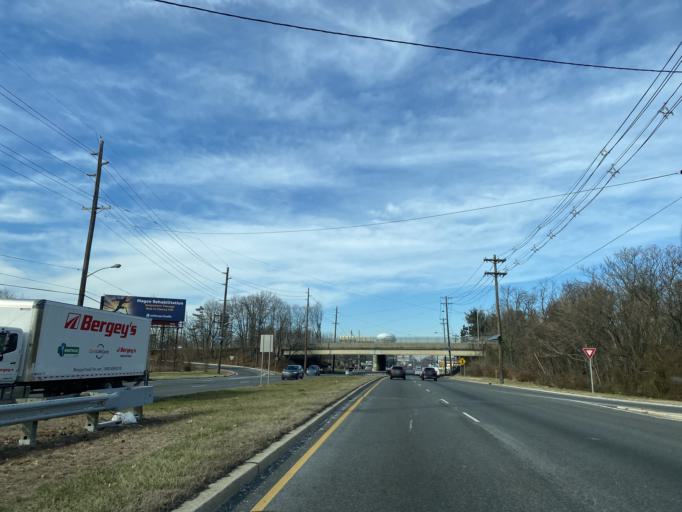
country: US
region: New Jersey
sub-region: Burlington County
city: Maple Shade
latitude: 39.9448
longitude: -74.9809
